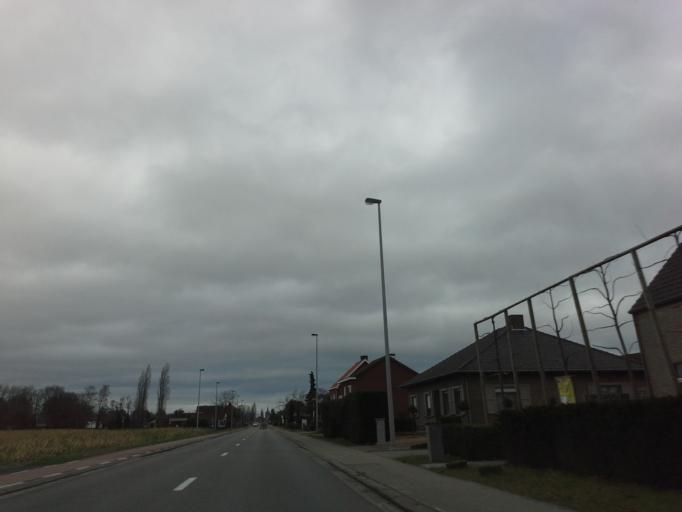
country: BE
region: Flanders
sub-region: Provincie Antwerpen
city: Olen
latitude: 51.1292
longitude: 4.8296
